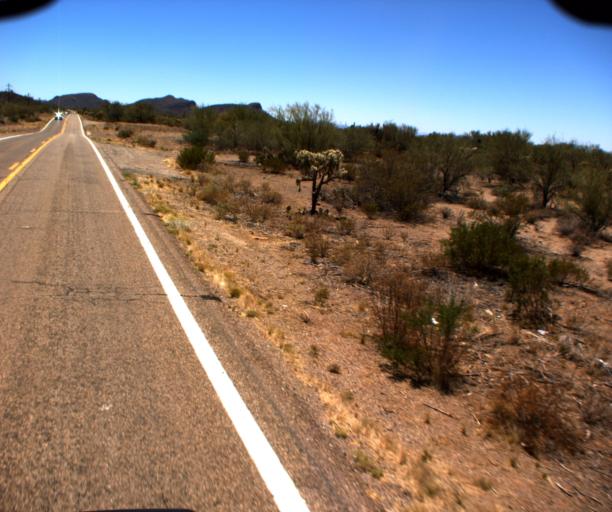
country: US
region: Arizona
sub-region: Pima County
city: Sells
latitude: 31.9939
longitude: -111.9804
